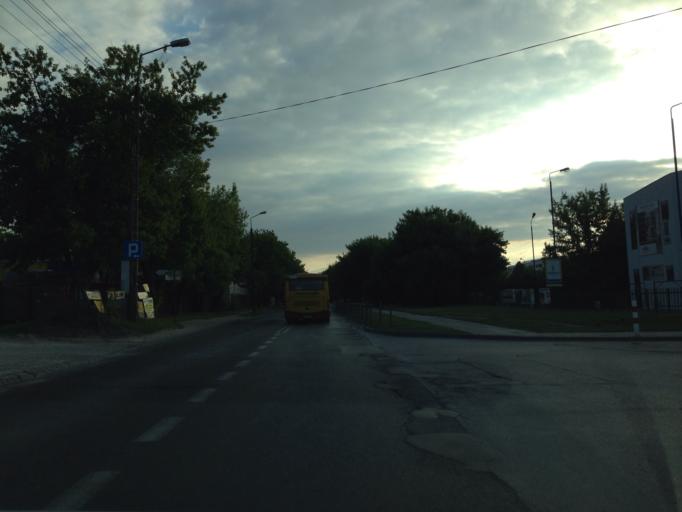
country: PL
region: Masovian Voivodeship
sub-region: Warszawa
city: Mokotow
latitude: 52.2130
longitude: 21.0542
